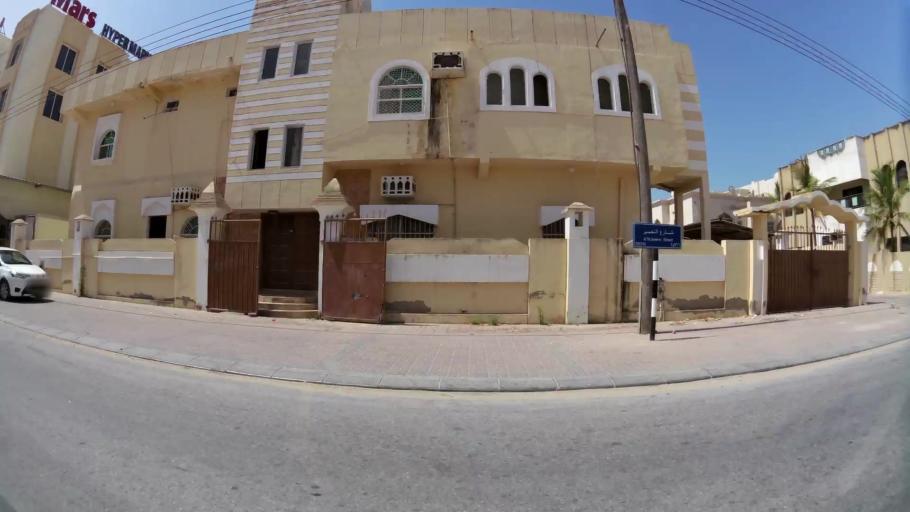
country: OM
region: Zufar
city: Salalah
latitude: 17.0193
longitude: 54.1044
